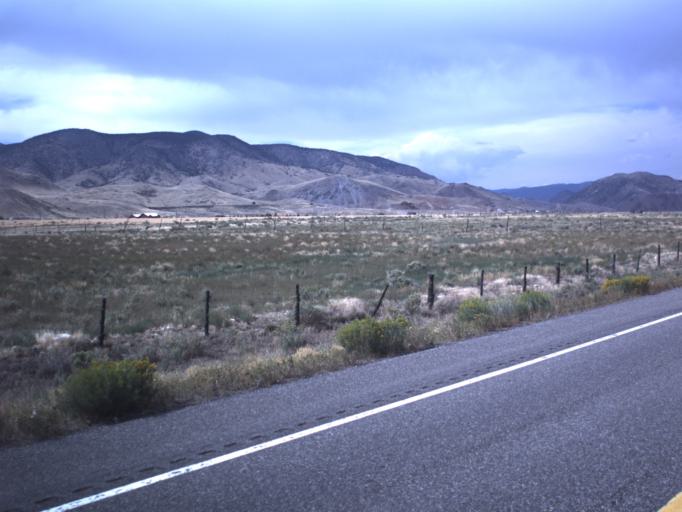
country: US
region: Utah
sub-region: Piute County
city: Junction
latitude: 38.4373
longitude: -112.2304
